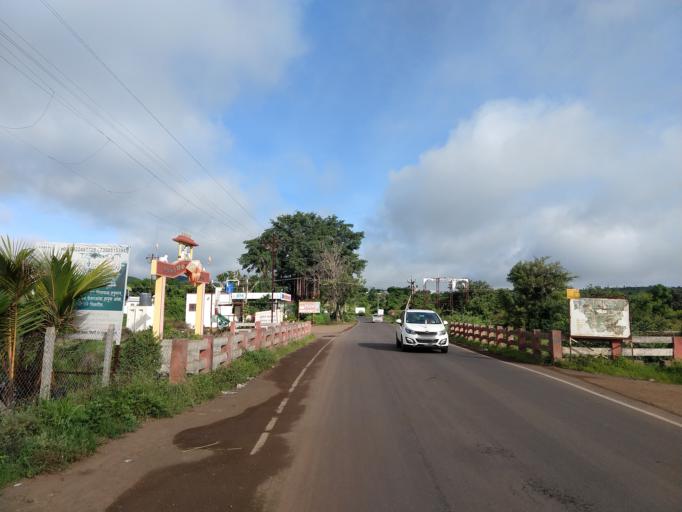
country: IN
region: Maharashtra
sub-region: Pune Division
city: Khed
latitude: 18.3935
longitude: 73.9203
